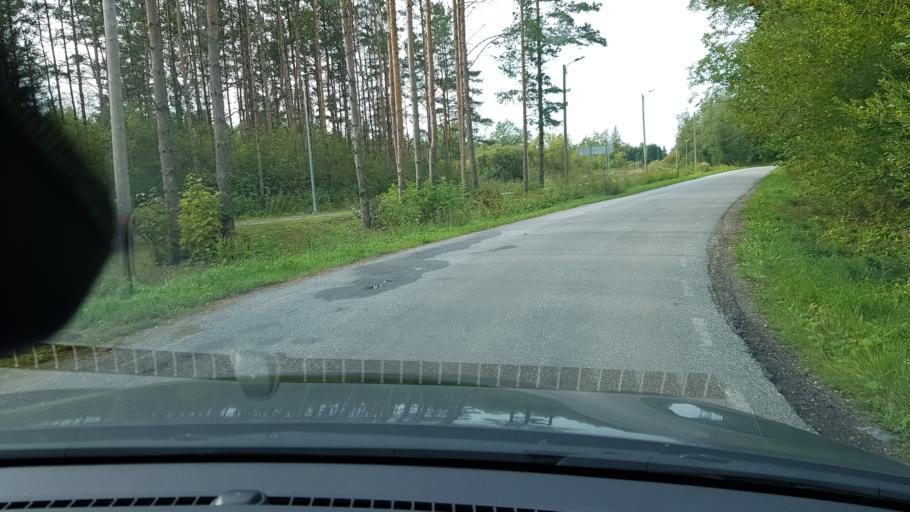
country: EE
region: Harju
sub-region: Raasiku vald
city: Raasiku
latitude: 59.4480
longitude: 25.1791
